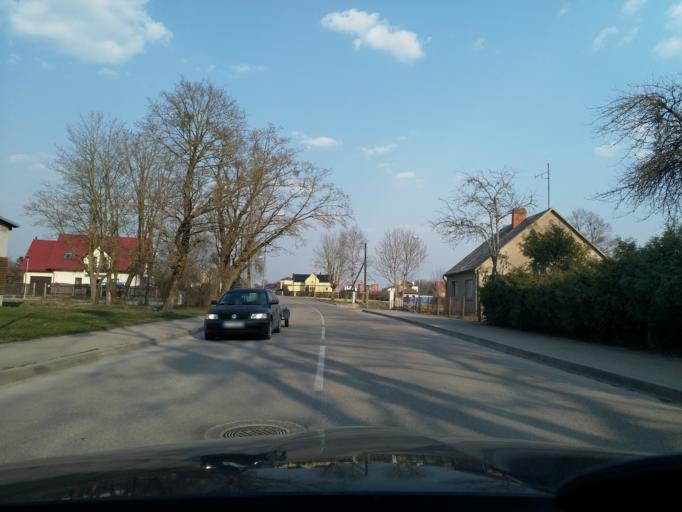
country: LV
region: Grobina
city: Grobina
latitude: 56.5339
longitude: 21.1815
